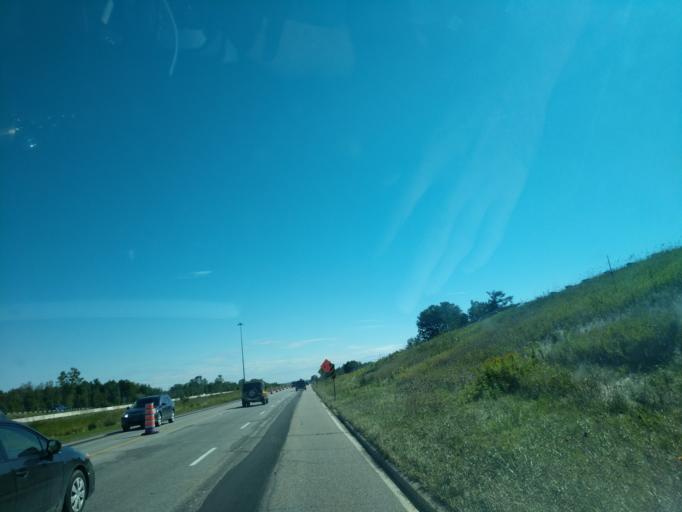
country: CA
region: Quebec
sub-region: Outaouais
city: Gatineau
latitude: 45.5111
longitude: -75.6440
